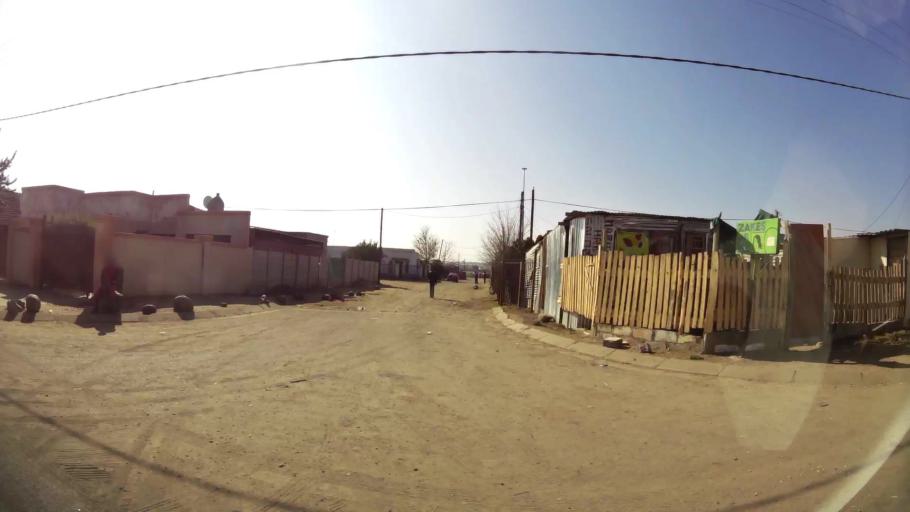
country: ZA
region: Orange Free State
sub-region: Mangaung Metropolitan Municipality
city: Bloemfontein
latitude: -29.1892
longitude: 26.2470
